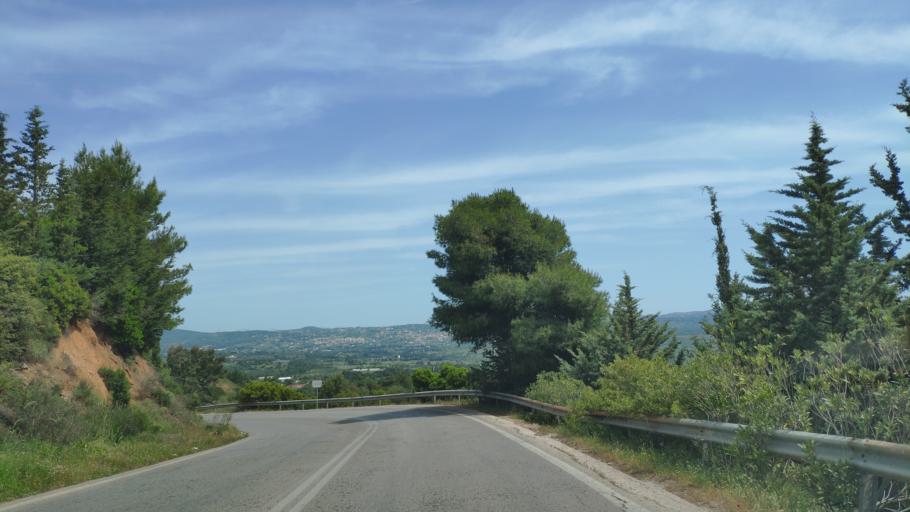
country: GR
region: Attica
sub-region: Nomarchia Anatolikis Attikis
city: Agios Stefanos
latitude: 38.1586
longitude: 23.8605
